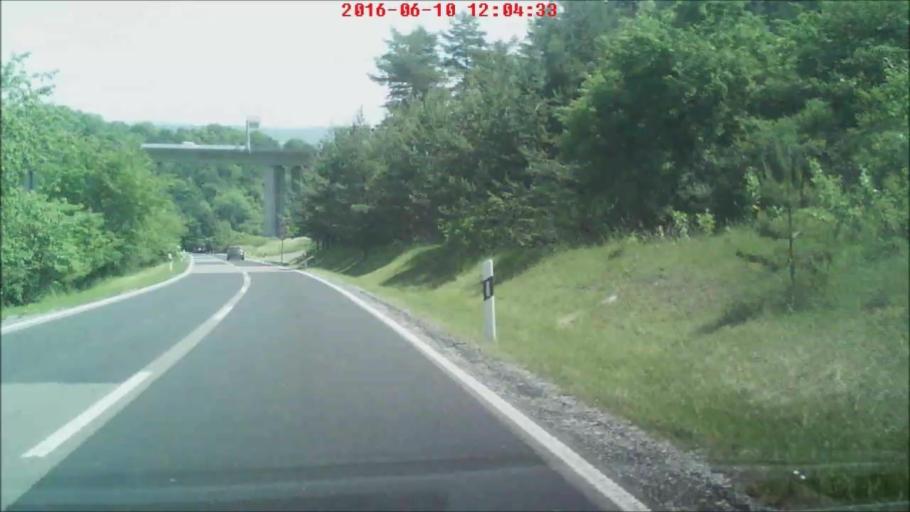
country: DE
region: Thuringia
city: Rohr
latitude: 50.5806
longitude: 10.4793
